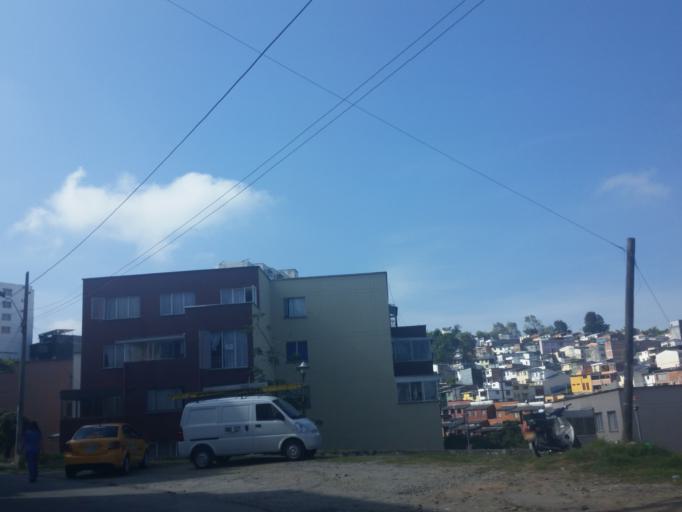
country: CO
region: Caldas
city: Manizales
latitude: 5.0809
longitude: -75.5245
